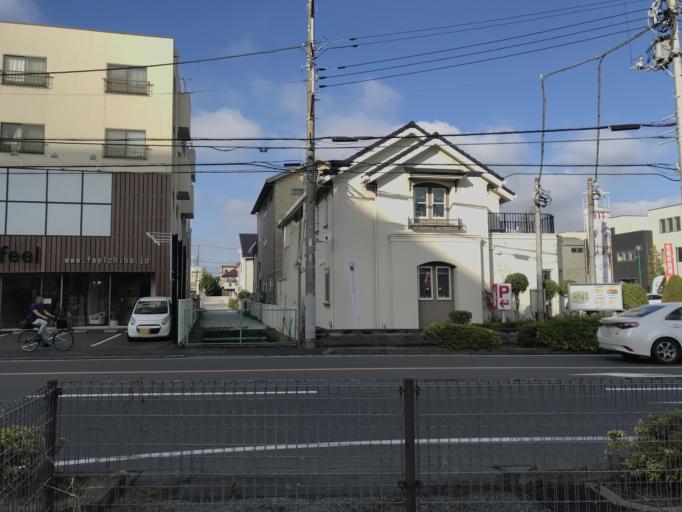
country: JP
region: Chiba
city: Funabashi
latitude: 35.7065
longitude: 139.9857
